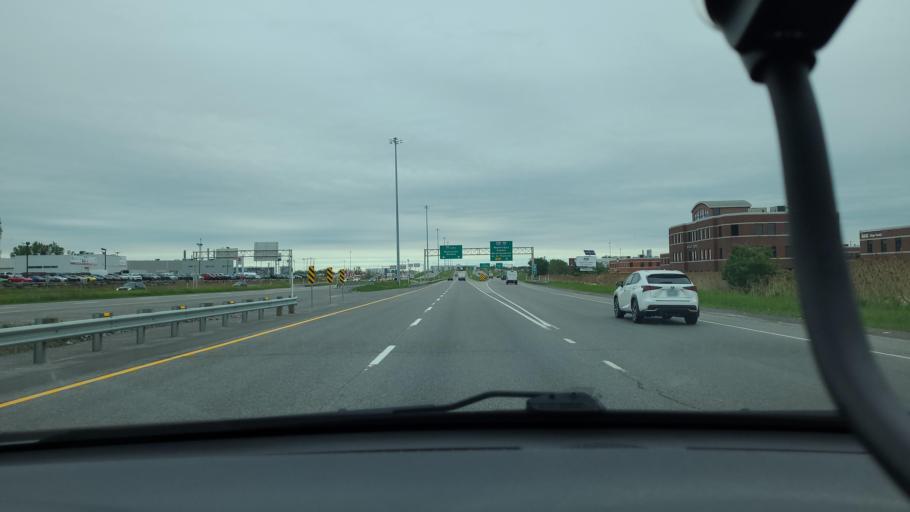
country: CA
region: Quebec
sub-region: Lanaudiere
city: Terrebonne
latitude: 45.7147
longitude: -73.6230
